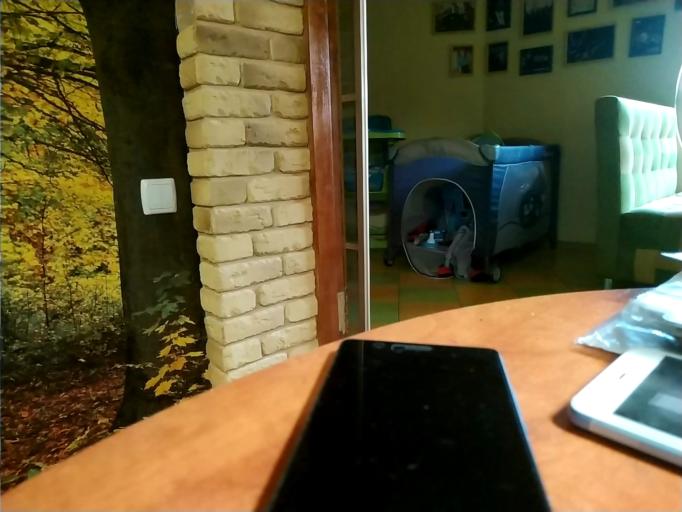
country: RU
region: Kaluga
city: Khvastovichi
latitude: 53.6640
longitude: 35.4451
